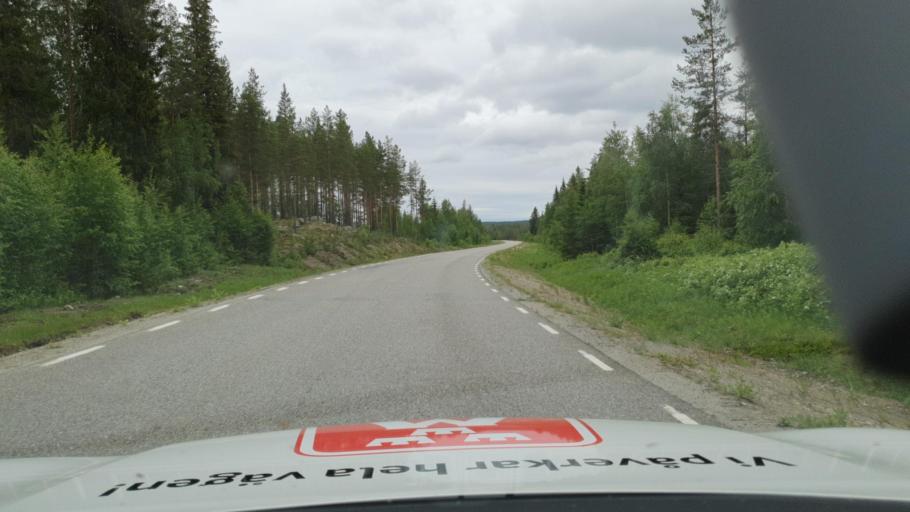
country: SE
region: Vaesterbotten
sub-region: Lycksele Kommun
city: Lycksele
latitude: 64.1887
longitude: 18.3137
